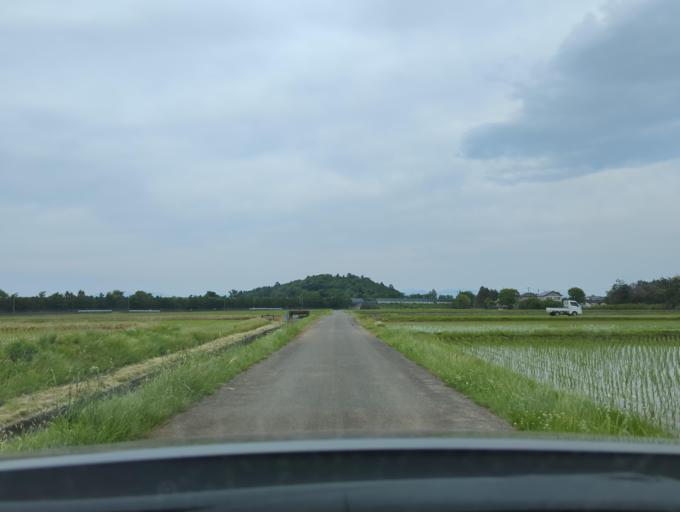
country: JP
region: Fukushima
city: Koriyama
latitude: 37.3850
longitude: 140.3088
